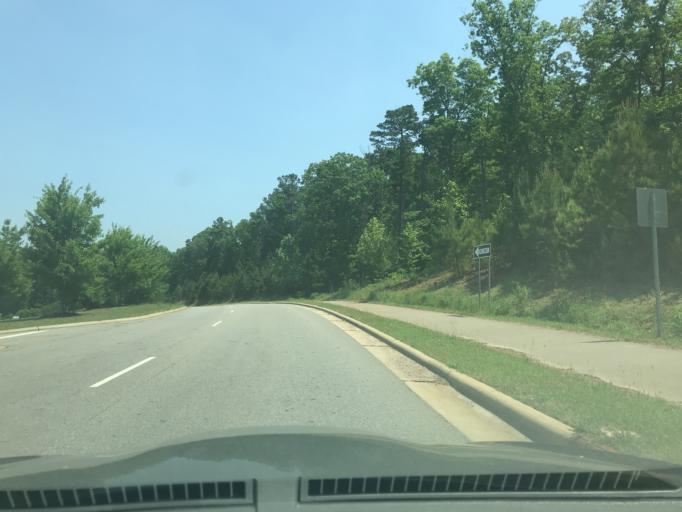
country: US
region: North Carolina
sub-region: Wake County
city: Cary
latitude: 35.7907
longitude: -78.7277
